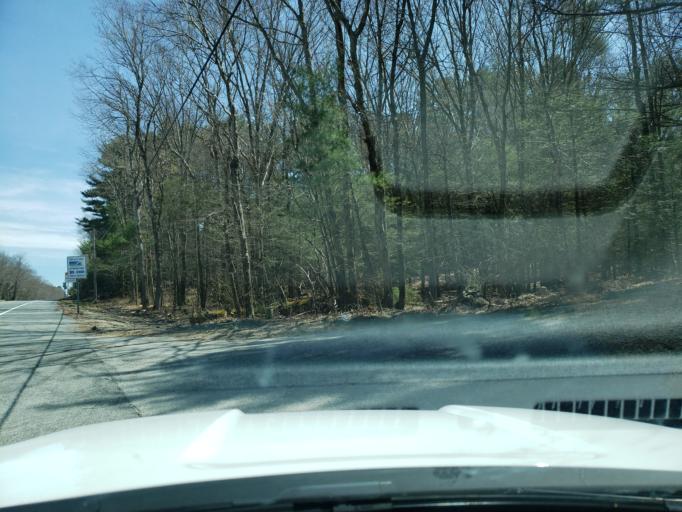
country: US
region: Rhode Island
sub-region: Providence County
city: Foster
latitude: 41.8493
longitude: -71.7935
